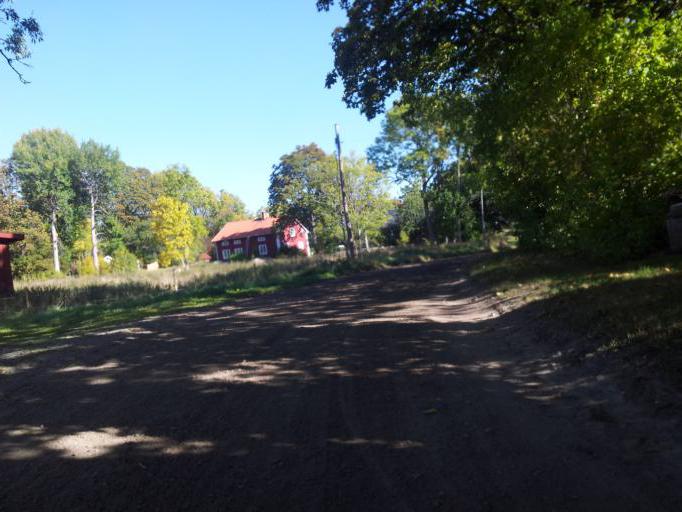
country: SE
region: Stockholm
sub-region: Norrtalje Kommun
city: Nykvarn
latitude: 59.9067
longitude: 18.2150
